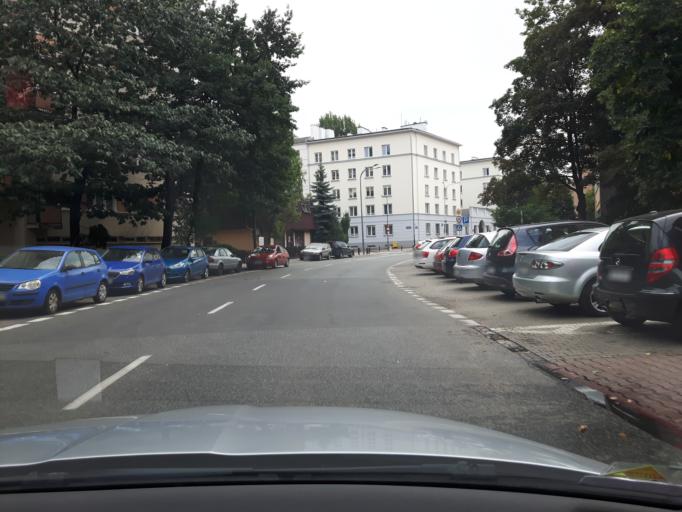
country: PL
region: Masovian Voivodeship
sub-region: Warszawa
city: Ochota
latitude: 52.2212
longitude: 20.9782
